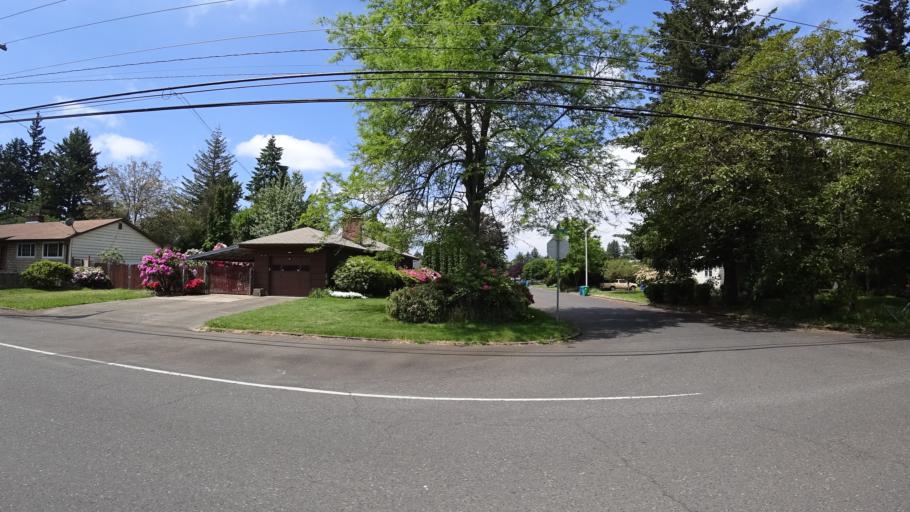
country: US
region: Oregon
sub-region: Multnomah County
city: Gresham
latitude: 45.5016
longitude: -122.4950
